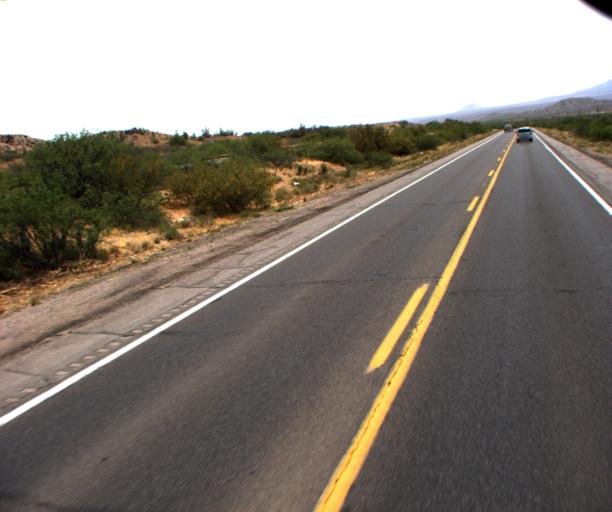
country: US
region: Arizona
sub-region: Gila County
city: Globe
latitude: 33.3631
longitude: -110.7085
